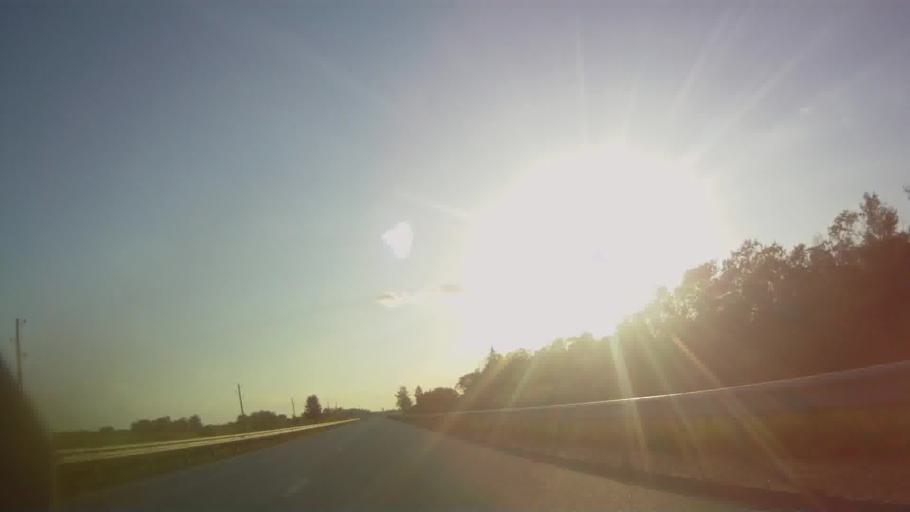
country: LV
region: Livani
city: Livani
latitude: 56.5350
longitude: 26.2837
